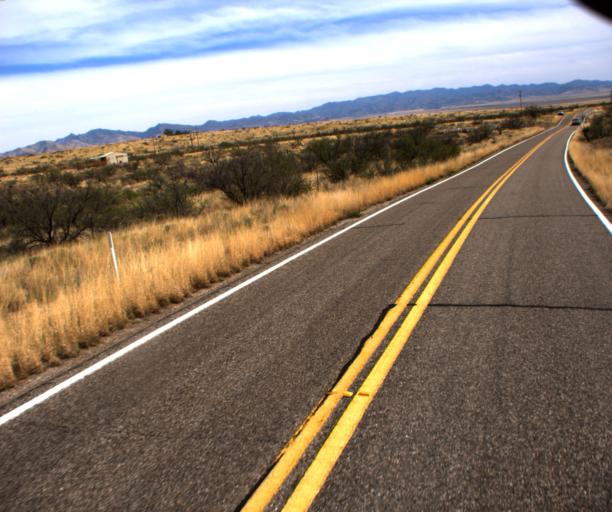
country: US
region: Arizona
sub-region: Cochise County
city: Willcox
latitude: 32.1327
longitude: -109.5594
